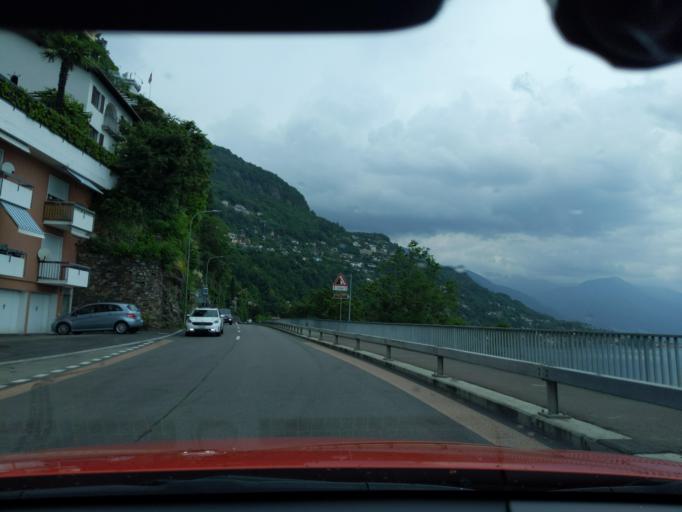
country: CH
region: Ticino
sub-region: Locarno District
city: Brissago
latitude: 46.1418
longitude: 8.7284
